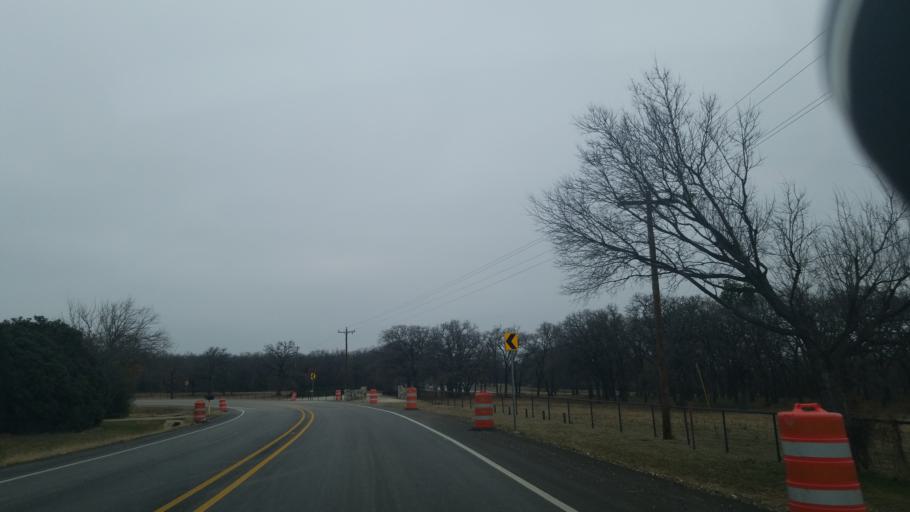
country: US
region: Texas
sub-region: Denton County
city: Argyle
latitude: 33.1276
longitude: -97.1395
